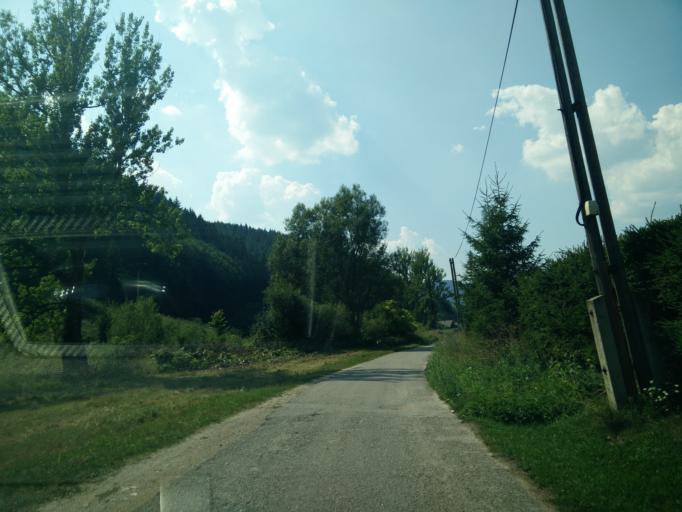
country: SK
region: Zilinsky
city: Rajec
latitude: 49.0377
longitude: 18.6529
